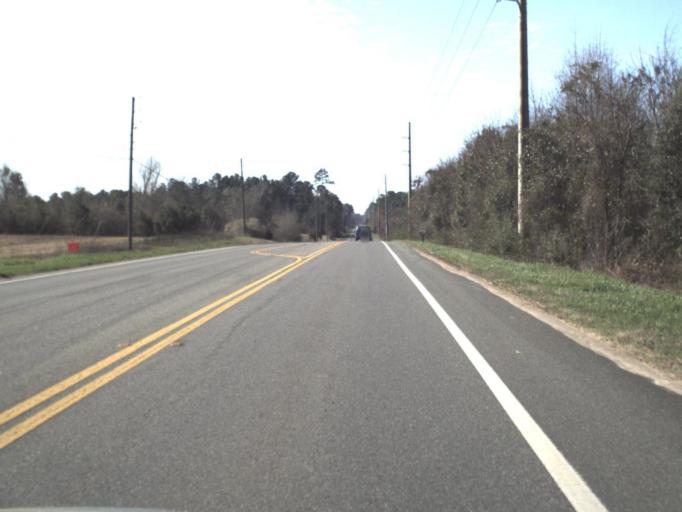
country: US
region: Florida
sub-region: Jackson County
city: Marianna
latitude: 30.8111
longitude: -85.1754
